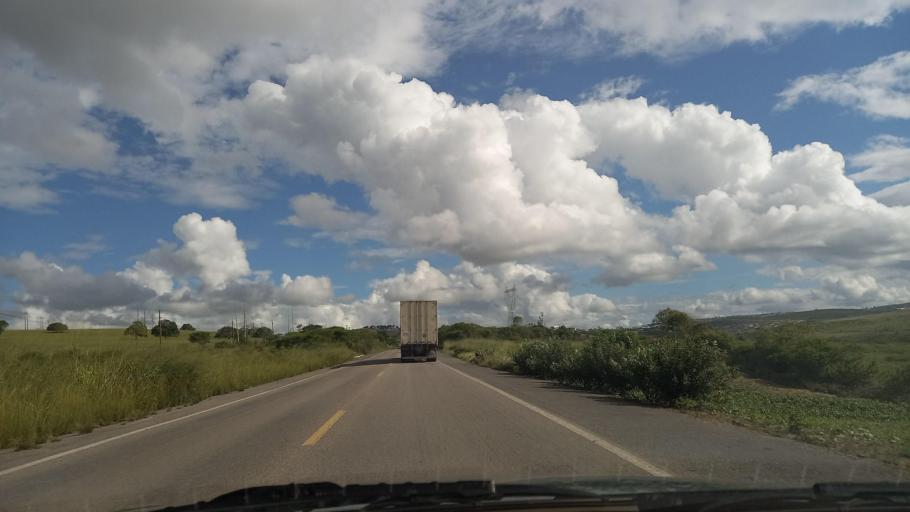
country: BR
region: Pernambuco
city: Garanhuns
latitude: -8.8464
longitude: -36.4596
